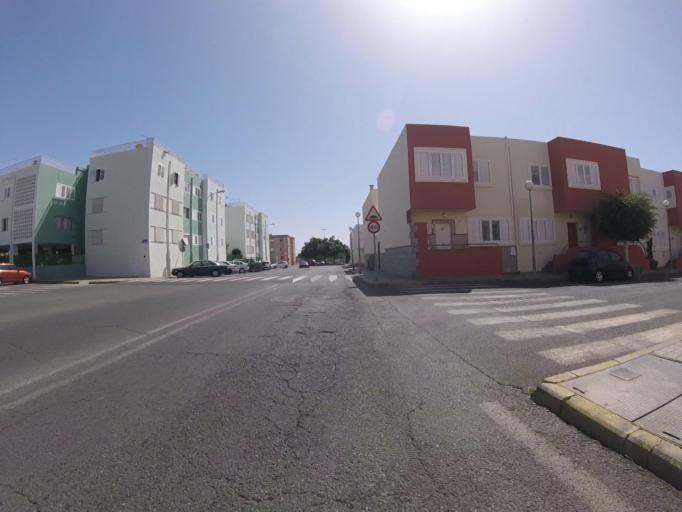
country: ES
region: Canary Islands
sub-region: Provincia de Las Palmas
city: Maspalomas
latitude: 27.7689
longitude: -15.5833
